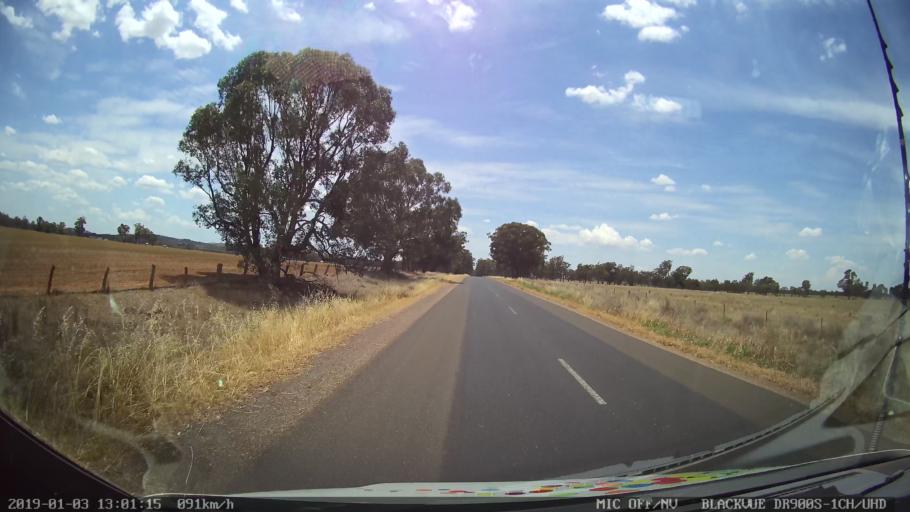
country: AU
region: New South Wales
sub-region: Cabonne
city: Canowindra
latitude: -33.6259
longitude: 148.4155
